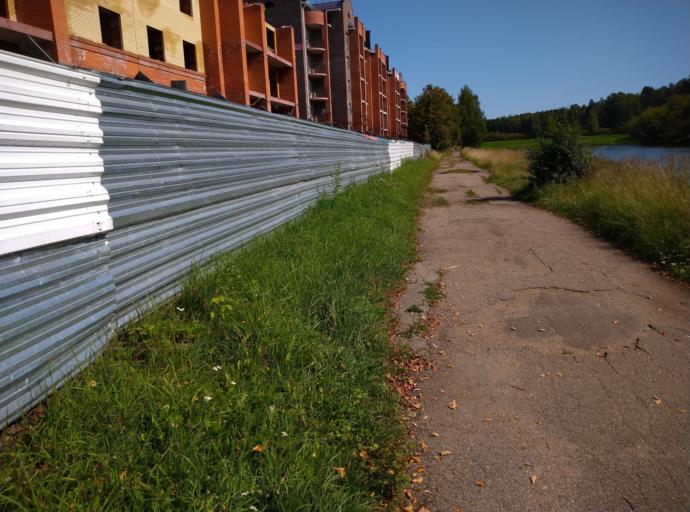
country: RU
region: Kostroma
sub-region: Kostromskoy Rayon
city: Kostroma
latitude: 57.7982
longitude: 40.9555
